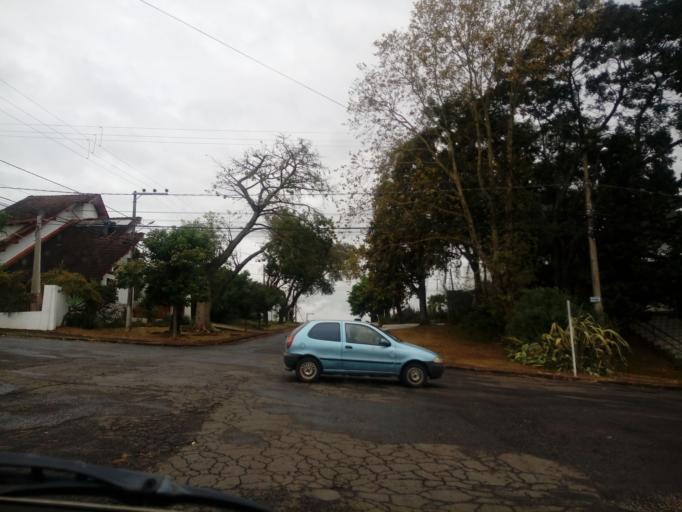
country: BR
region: Santa Catarina
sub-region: Chapeco
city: Chapeco
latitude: -27.1084
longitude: -52.6228
